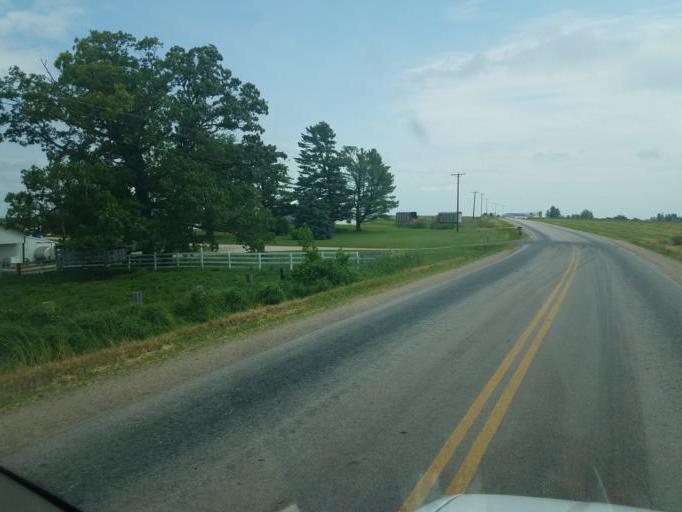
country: US
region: Wisconsin
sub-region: Monroe County
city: Cashton
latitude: 43.7552
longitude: -90.7498
